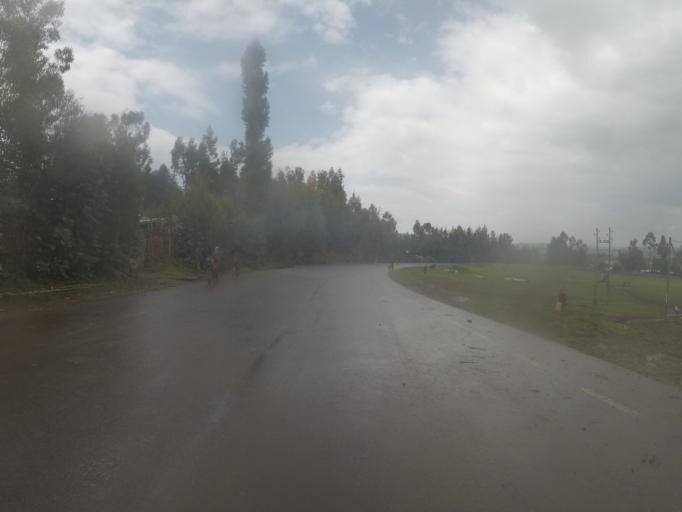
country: ET
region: Amhara
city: Debark'
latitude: 13.1057
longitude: 37.8562
